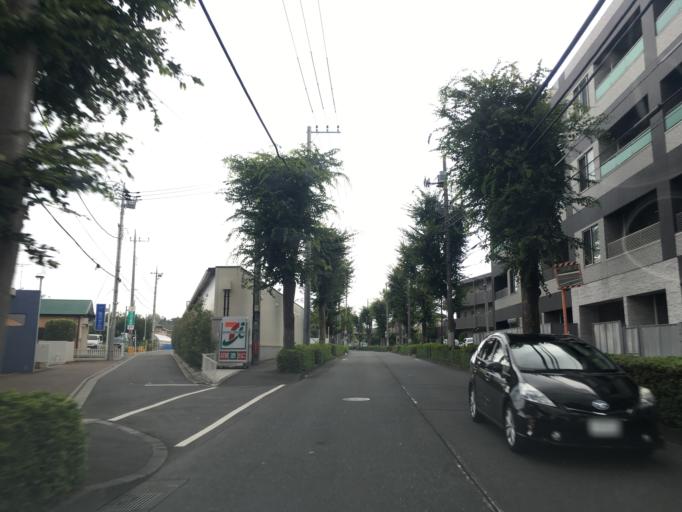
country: JP
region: Tokyo
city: Kokubunji
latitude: 35.6736
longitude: 139.5057
